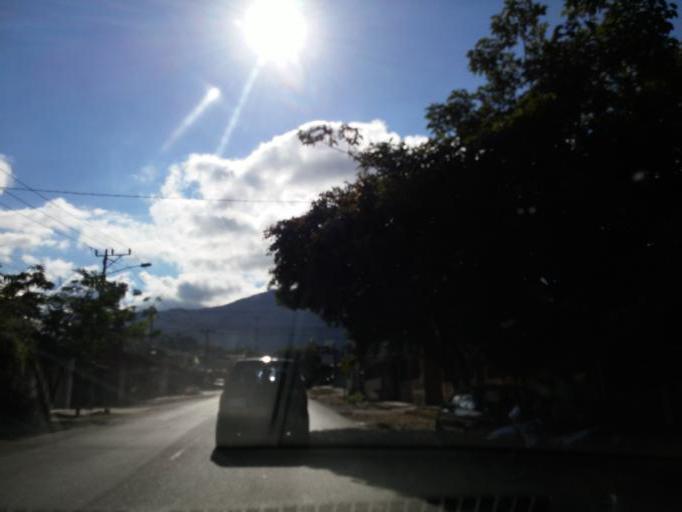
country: CR
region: San Jose
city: San Rafael Arriba
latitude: 9.8703
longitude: -84.0816
